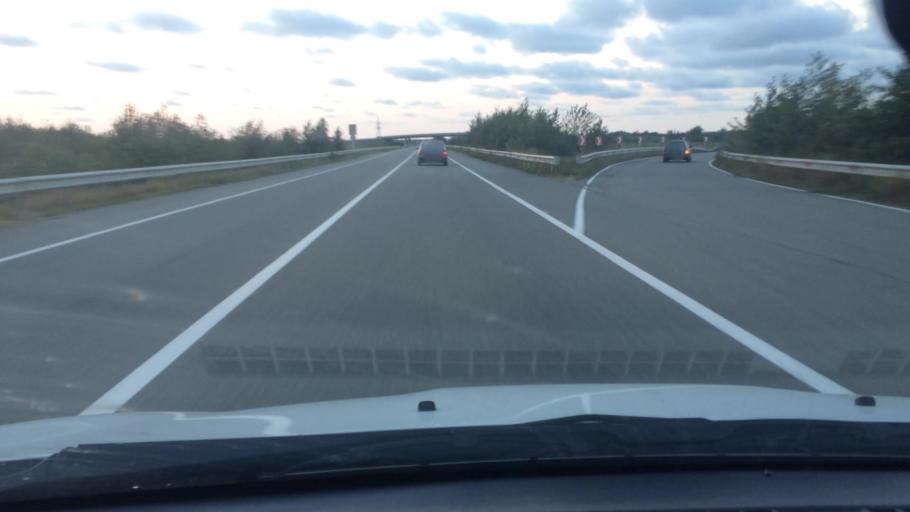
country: GE
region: Ajaria
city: Ochkhamuri
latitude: 41.8949
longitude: 41.8018
